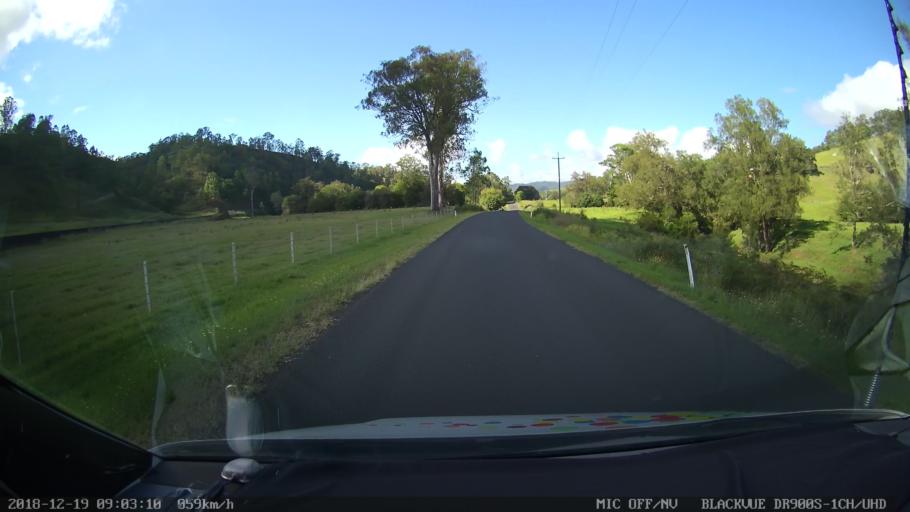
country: AU
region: New South Wales
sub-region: Kyogle
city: Kyogle
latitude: -28.4452
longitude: 152.9521
